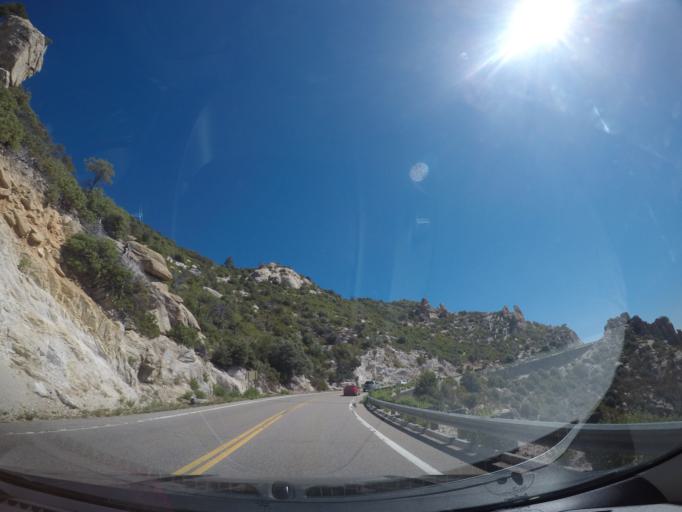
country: US
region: Arizona
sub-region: Pima County
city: Tanque Verde
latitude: 32.3783
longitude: -110.6999
